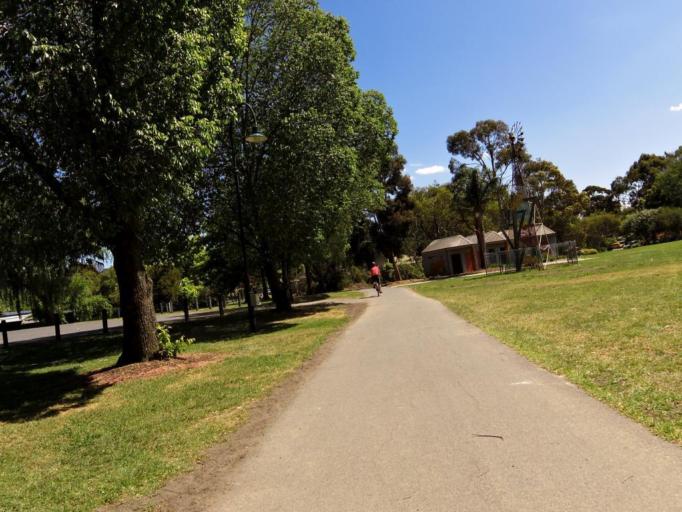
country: AU
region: Victoria
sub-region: Knox
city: Ferntree Gully
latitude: -37.8903
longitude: 145.2919
